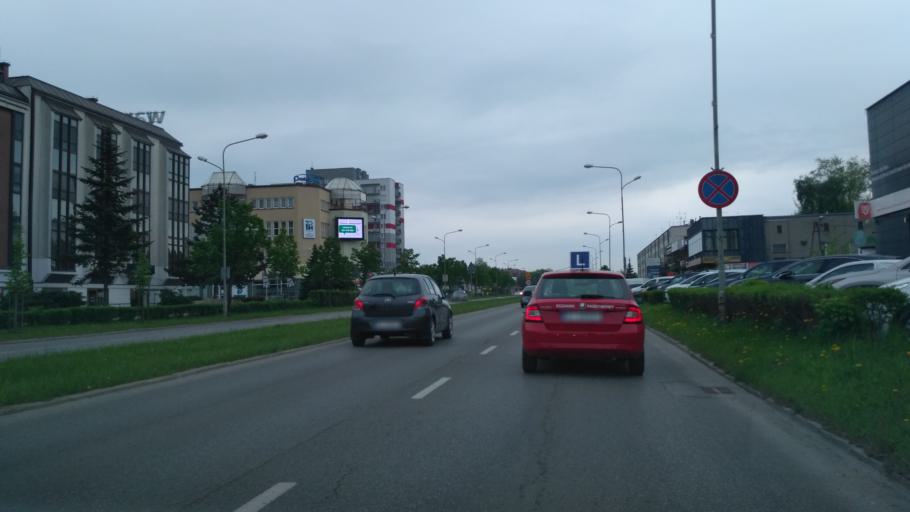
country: PL
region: Lesser Poland Voivodeship
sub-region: Powiat tarnowski
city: Tarnow
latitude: 50.0178
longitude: 21.0000
